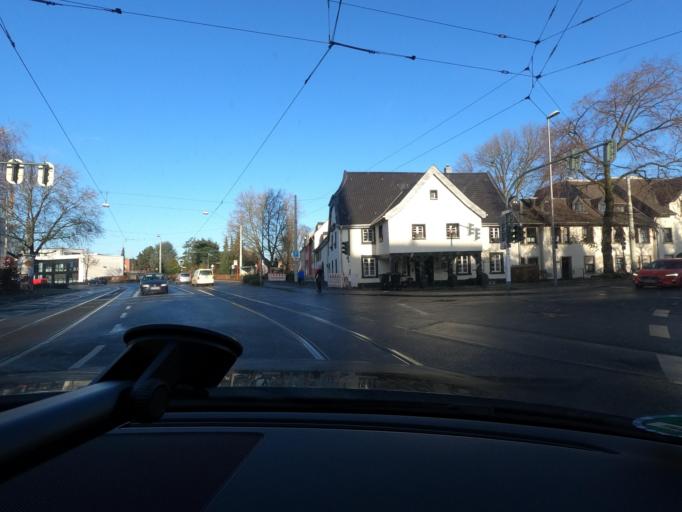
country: DE
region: North Rhine-Westphalia
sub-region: Regierungsbezirk Dusseldorf
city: Krefeld
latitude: 51.3477
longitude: 6.6187
